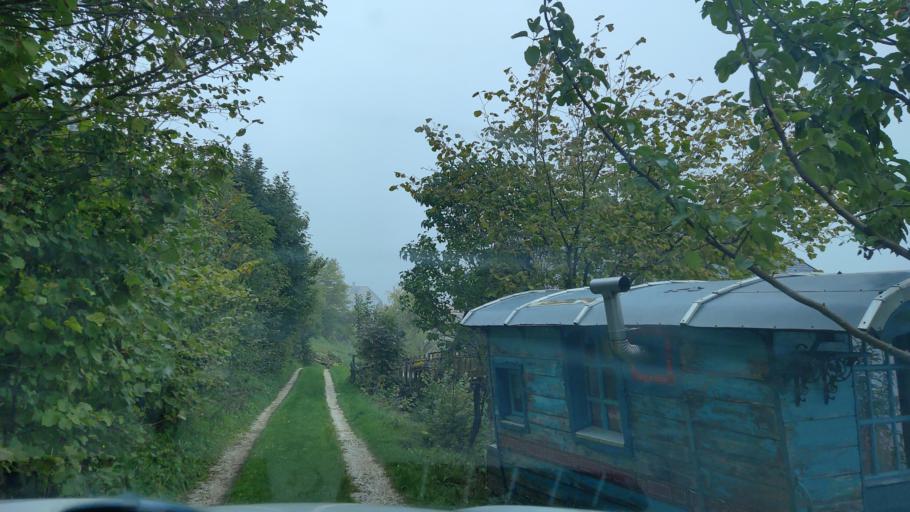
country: FR
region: Rhone-Alpes
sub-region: Departement de la Savoie
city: Les Echelles
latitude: 45.4124
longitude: 5.8388
